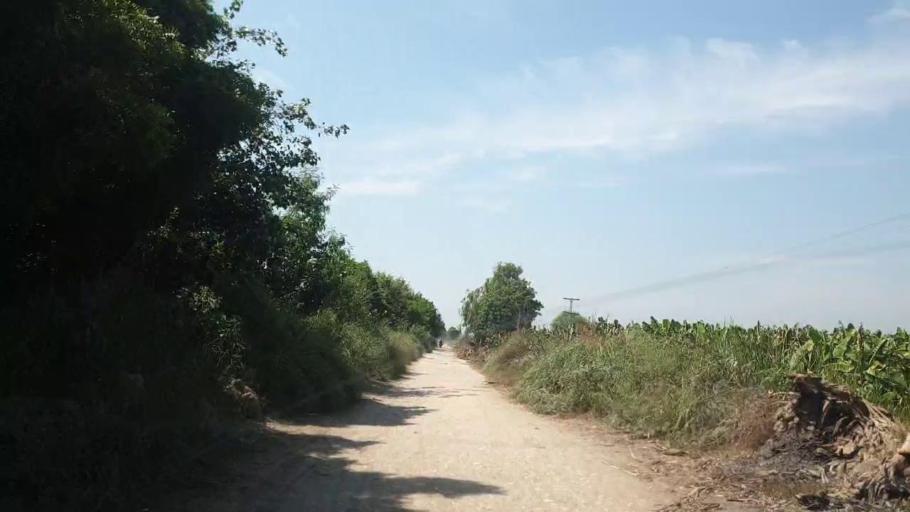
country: PK
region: Sindh
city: Tando Jam
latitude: 25.3991
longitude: 68.6135
